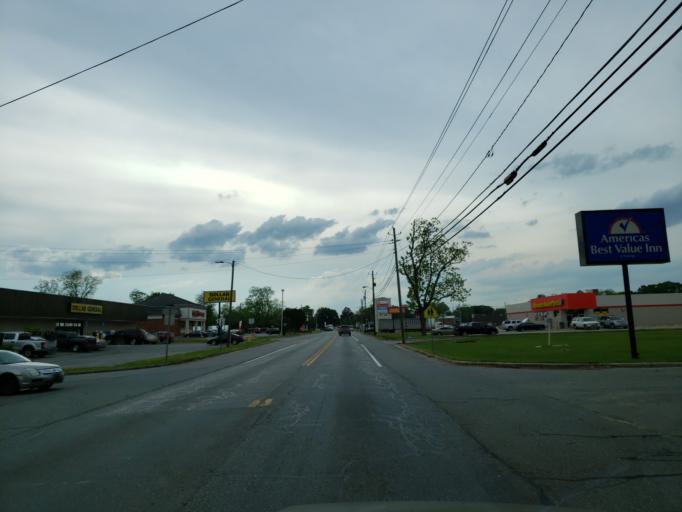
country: US
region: Georgia
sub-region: Macon County
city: Montezuma
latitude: 32.2935
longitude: -84.0168
